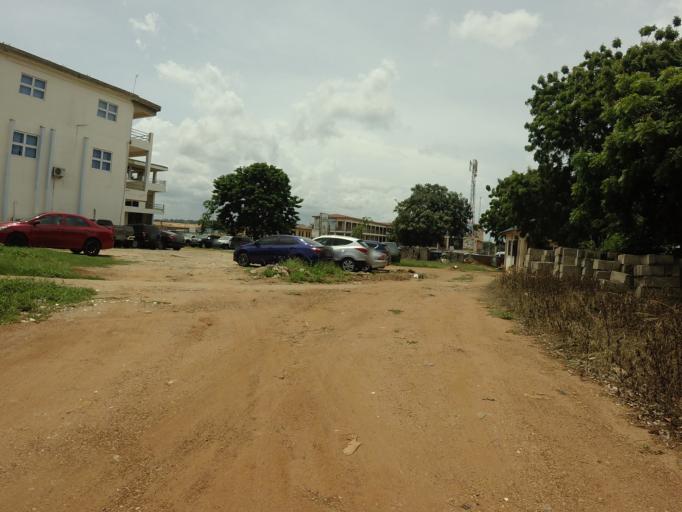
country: GH
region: Greater Accra
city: Accra
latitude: 5.5954
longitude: -0.2226
